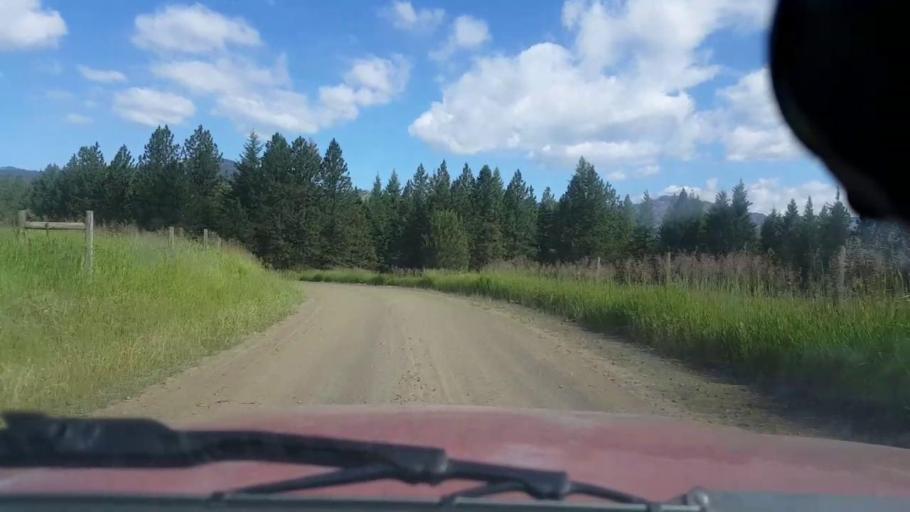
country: US
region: Washington
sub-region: Asotin County
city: Asotin
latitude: 46.0355
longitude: -117.4081
